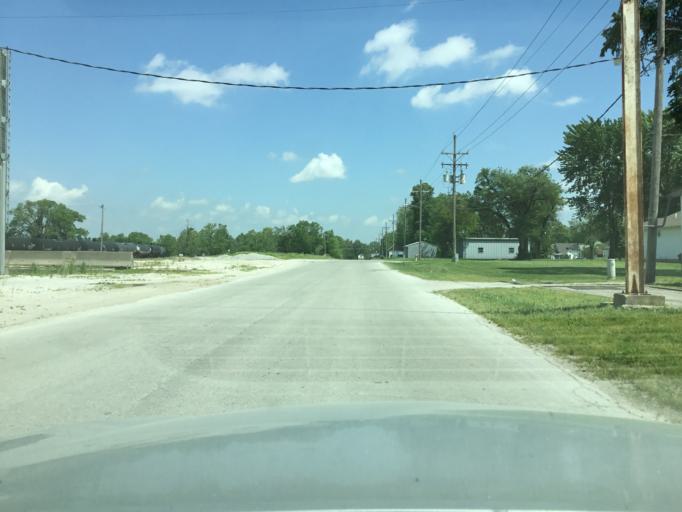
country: US
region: Kansas
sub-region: Labette County
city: Parsons
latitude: 37.3439
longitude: -95.2657
